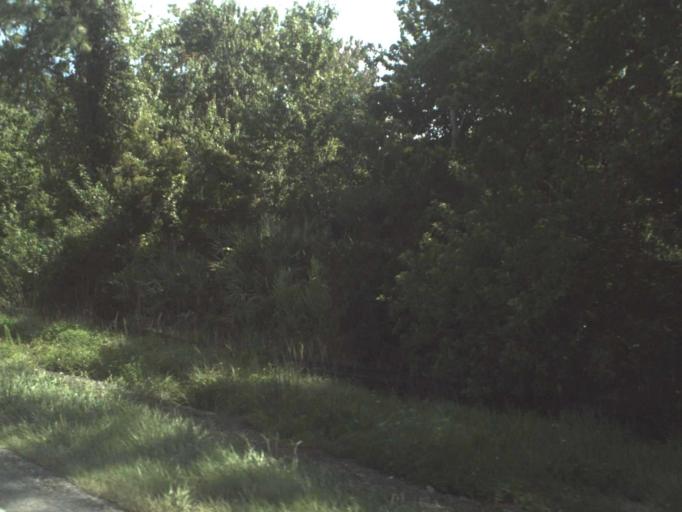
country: US
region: Florida
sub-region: Indian River County
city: Fellsmere
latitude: 27.7363
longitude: -80.5481
